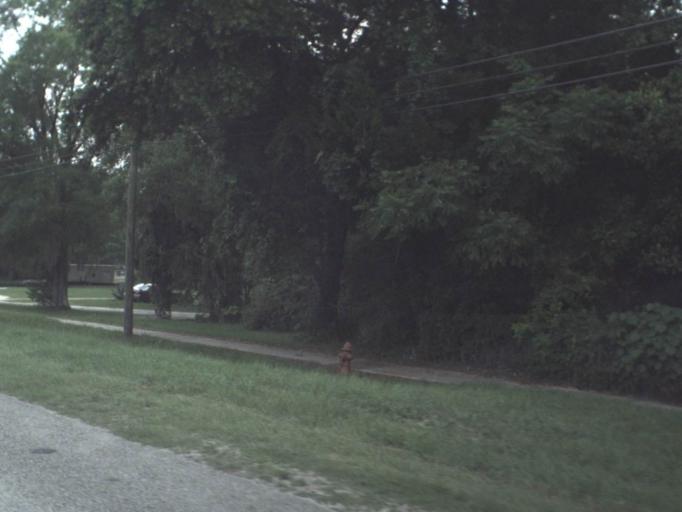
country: US
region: Florida
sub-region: Bradford County
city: Starke
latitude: 29.9296
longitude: -82.1208
